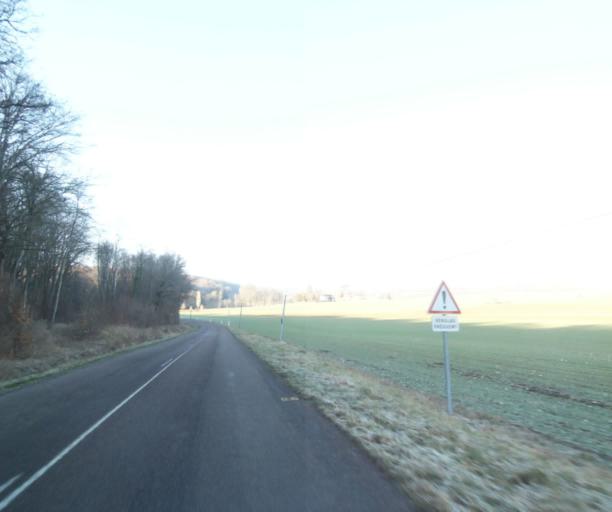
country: FR
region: Champagne-Ardenne
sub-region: Departement de la Haute-Marne
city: Chevillon
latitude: 48.5533
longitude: 5.0909
